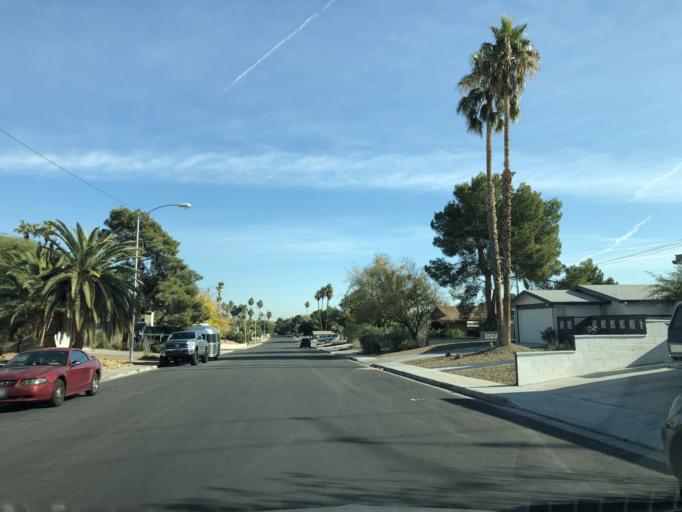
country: US
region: Nevada
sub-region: Clark County
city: Winchester
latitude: 36.1264
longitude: -115.1321
